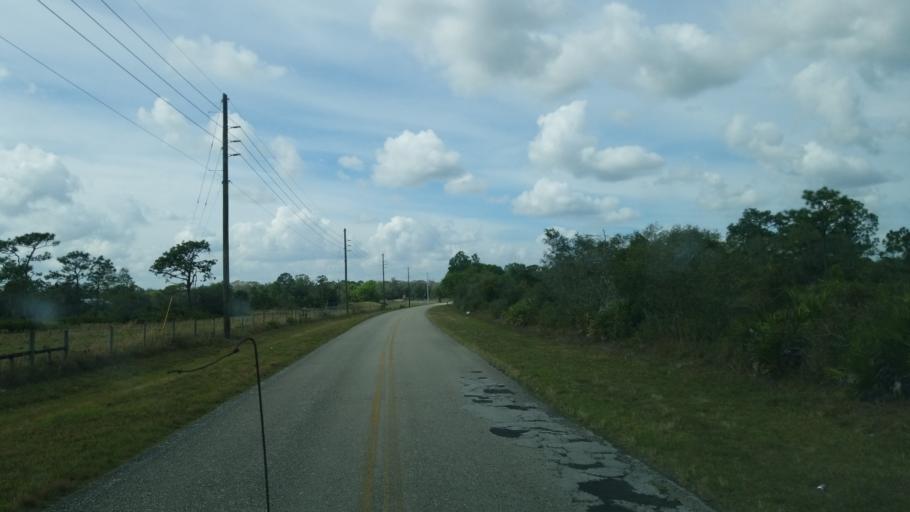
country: US
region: Florida
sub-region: Okeechobee County
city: Cypress Quarters
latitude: 27.5194
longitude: -80.7909
